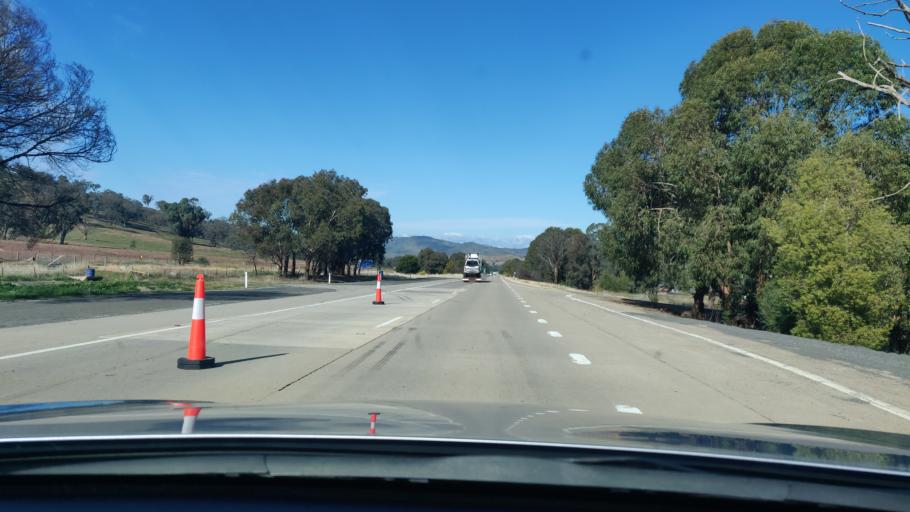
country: AU
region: New South Wales
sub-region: Gundagai
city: Gundagai
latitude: -35.0191
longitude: 148.1103
